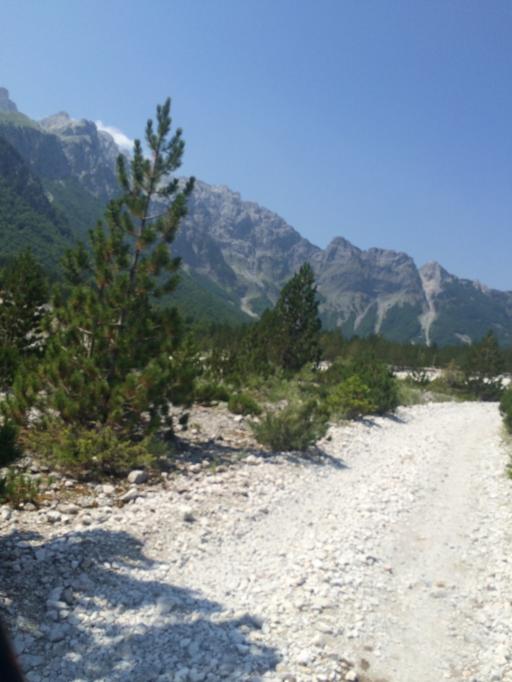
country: AL
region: Kukes
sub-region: Rrethi i Tropojes
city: Valbone
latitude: 42.4157
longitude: 19.8564
